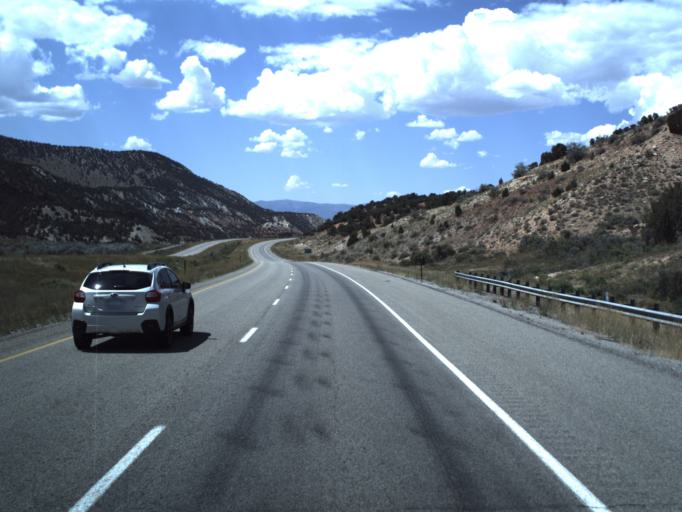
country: US
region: Utah
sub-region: Sevier County
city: Salina
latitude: 38.9205
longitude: -111.7551
